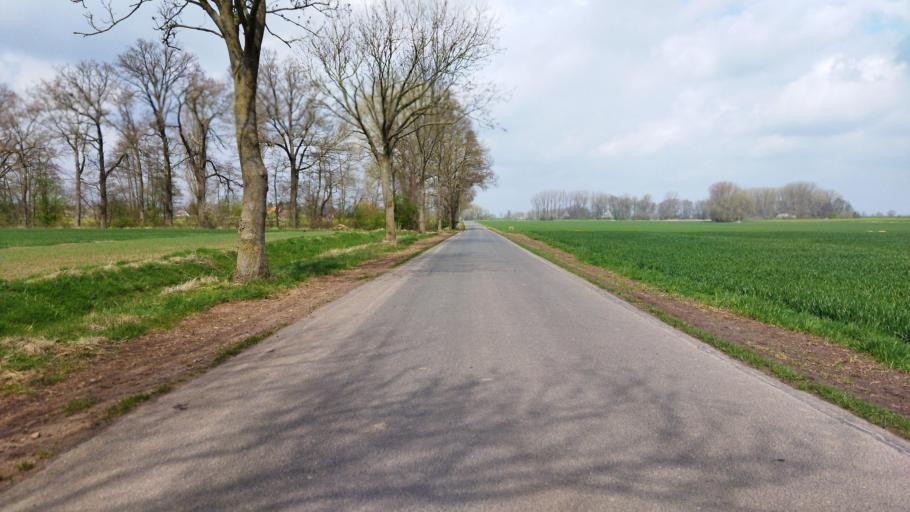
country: DE
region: Lower Saxony
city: Hilgermissen
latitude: 52.8406
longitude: 9.1898
